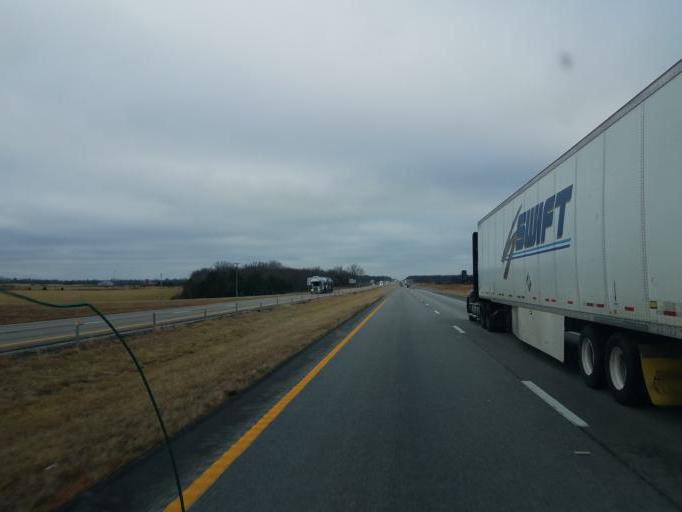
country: US
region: Missouri
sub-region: Webster County
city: Marshfield
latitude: 37.5030
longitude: -92.8424
